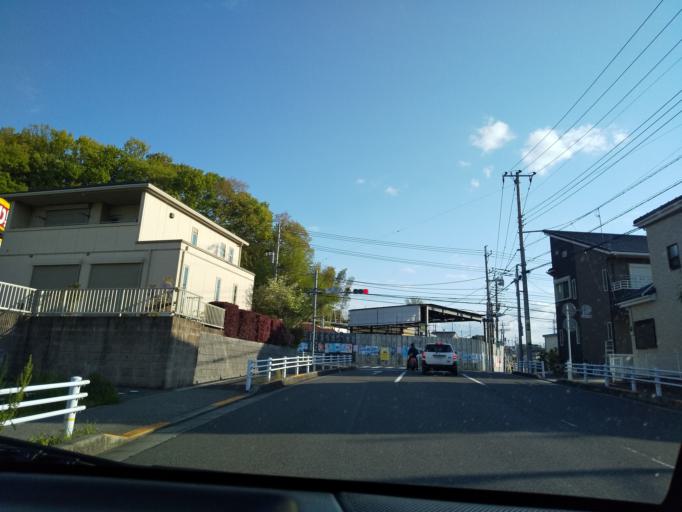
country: JP
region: Tokyo
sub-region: Machida-shi
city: Machida
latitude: 35.5883
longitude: 139.4549
